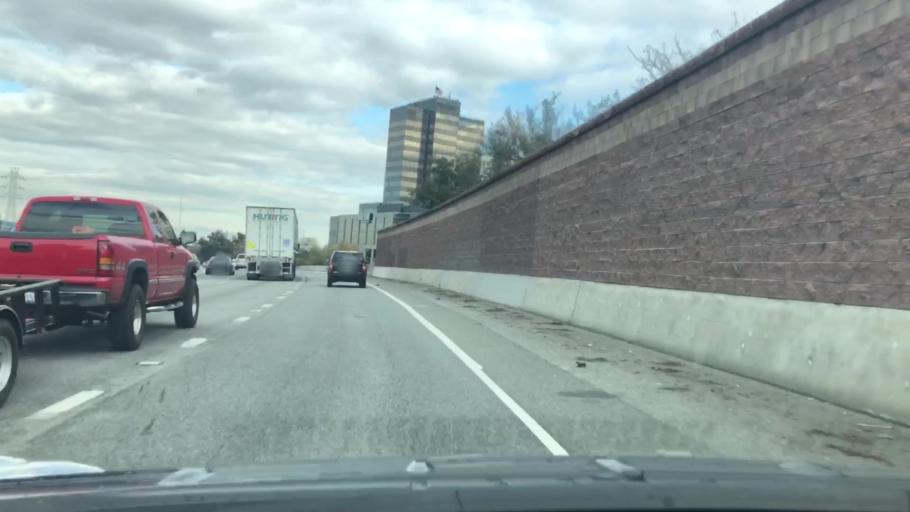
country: US
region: California
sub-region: Santa Clara County
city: Campbell
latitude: 37.2833
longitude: -121.9257
